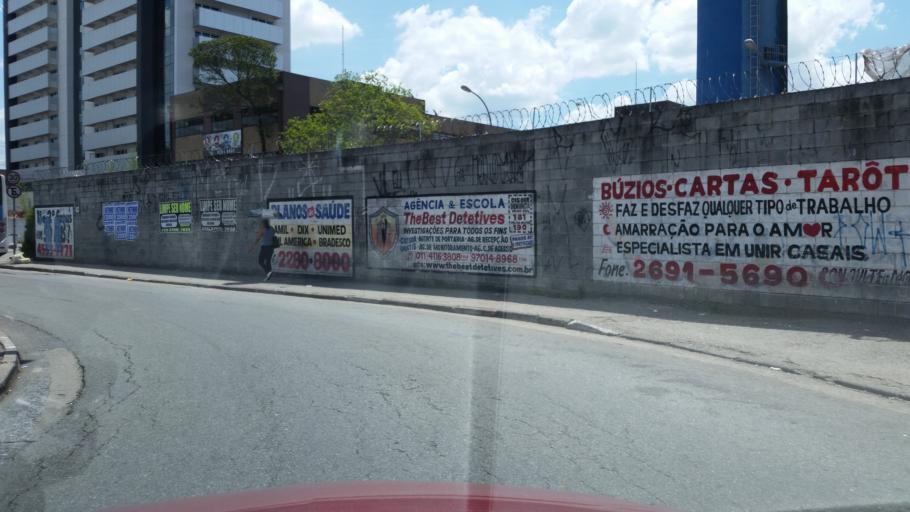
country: BR
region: Sao Paulo
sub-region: Diadema
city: Diadema
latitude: -23.6630
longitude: -46.7083
